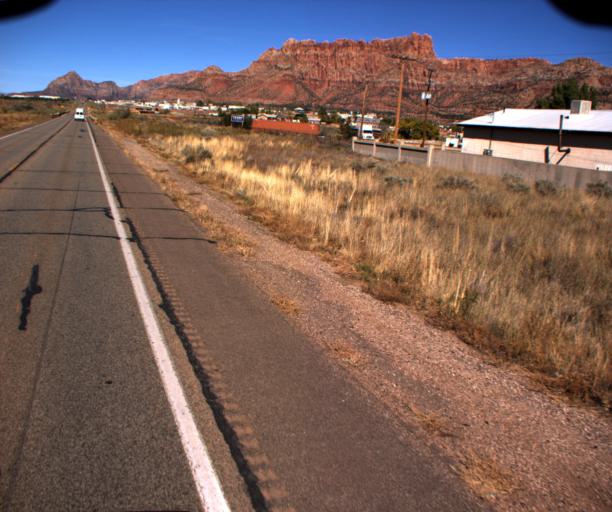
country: US
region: Arizona
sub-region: Mohave County
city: Colorado City
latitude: 36.9861
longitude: -112.9875
